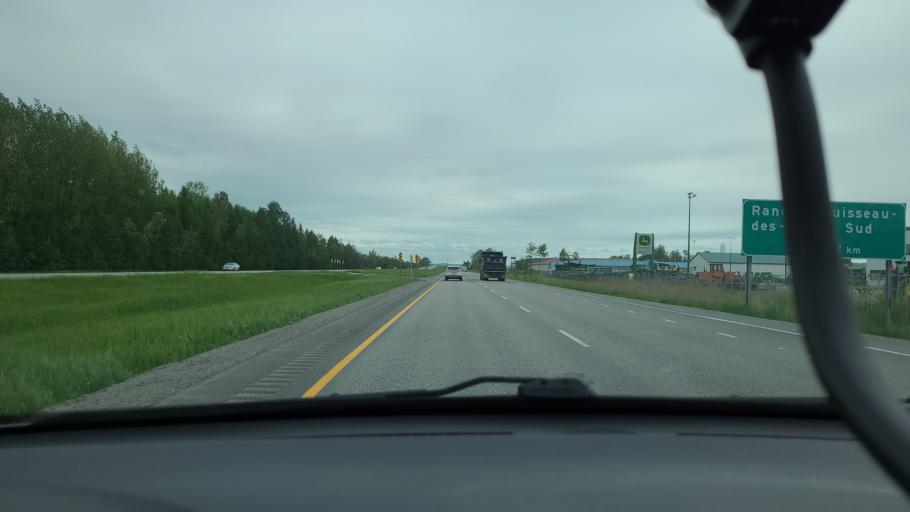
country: CA
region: Quebec
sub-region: Lanaudiere
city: Mascouche
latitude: 45.8269
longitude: -73.6093
